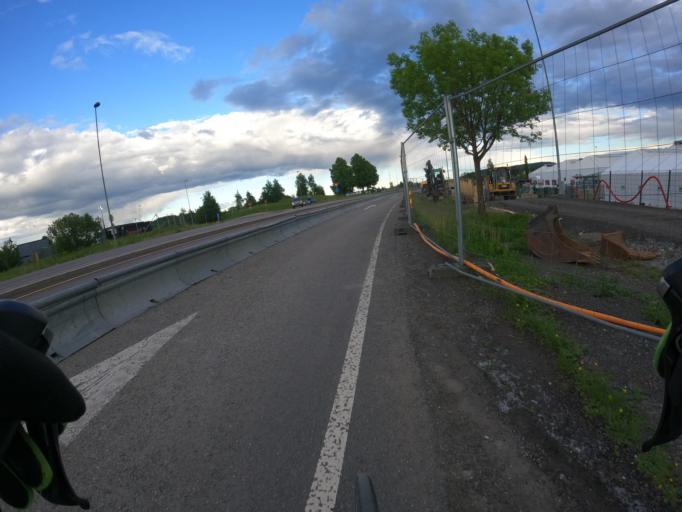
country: NO
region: Akershus
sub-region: Lorenskog
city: Kjenn
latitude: 59.9805
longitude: 10.9916
